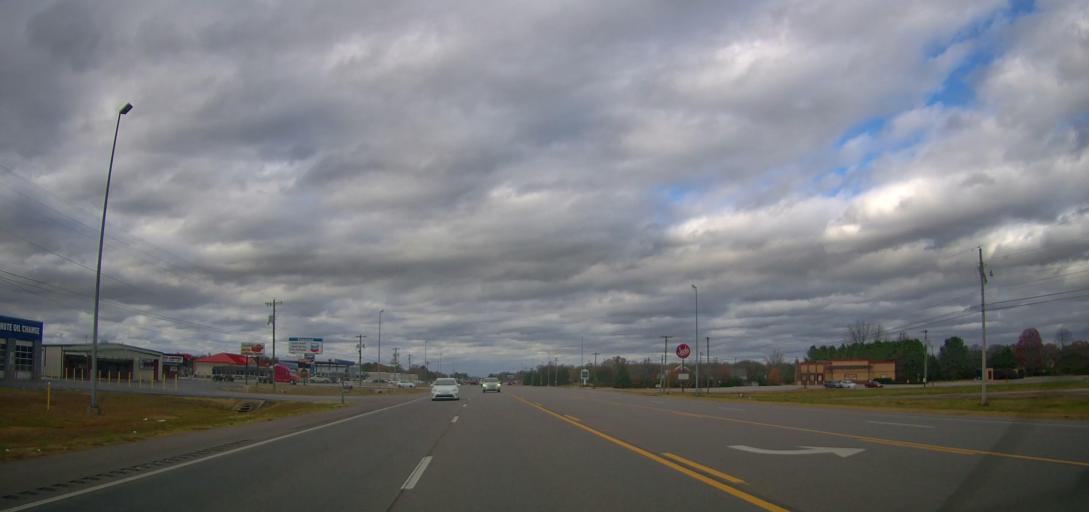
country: US
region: Alabama
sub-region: Lawrence County
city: Moulton
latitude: 34.4791
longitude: -87.2716
